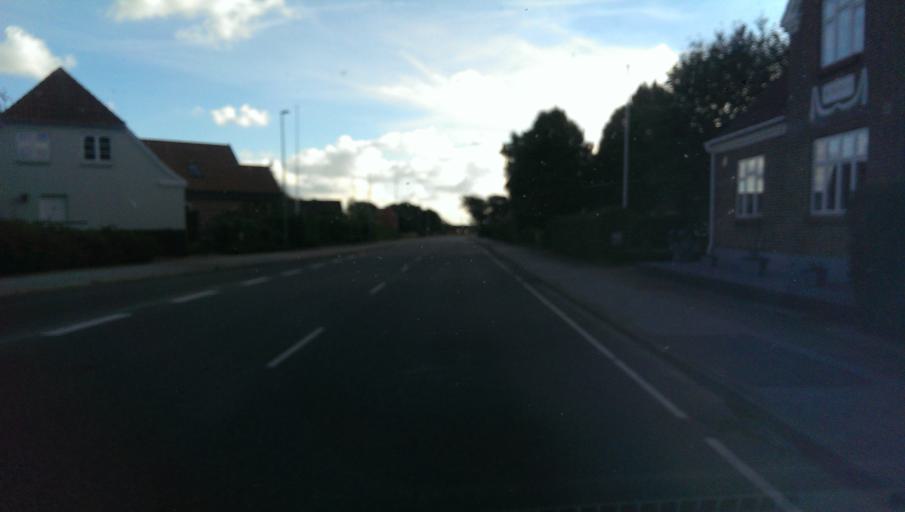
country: DK
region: South Denmark
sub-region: Esbjerg Kommune
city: Tjaereborg
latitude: 55.5092
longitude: 8.5577
